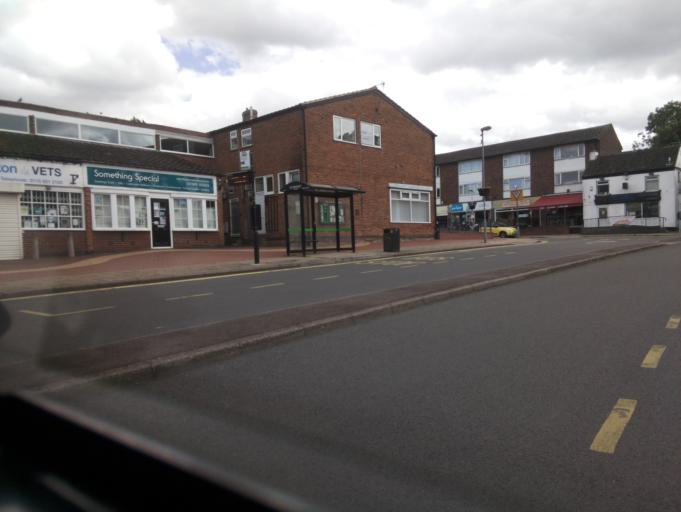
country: GB
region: England
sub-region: Nottinghamshire
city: East Leake
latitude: 52.8318
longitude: -1.1774
